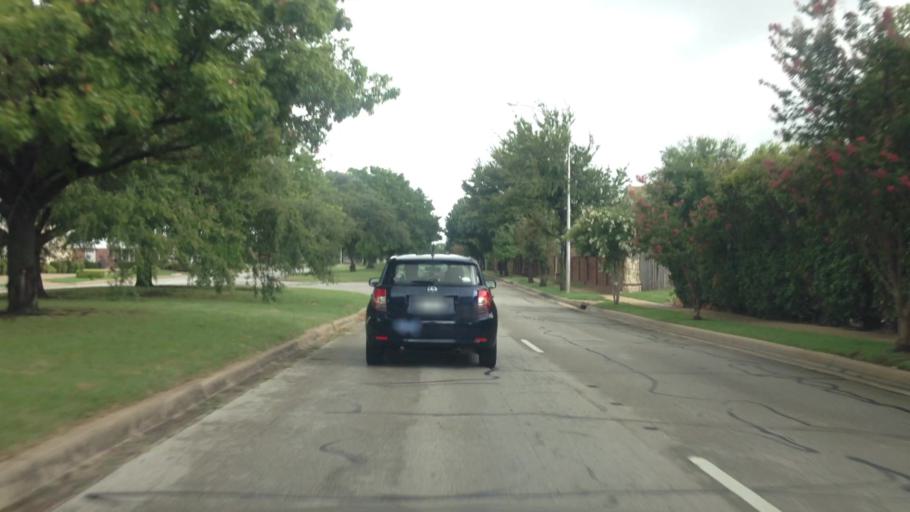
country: US
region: Texas
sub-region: Tarrant County
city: Edgecliff Village
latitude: 32.6374
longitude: -97.3946
